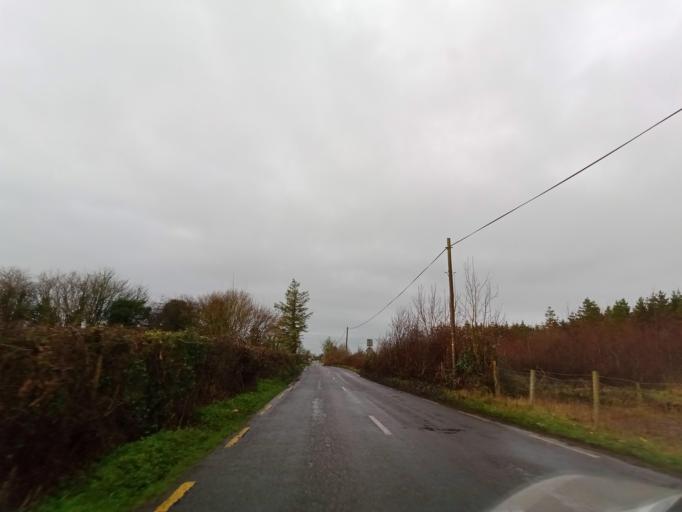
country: IE
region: Leinster
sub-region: Kilkenny
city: Callan
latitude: 52.5701
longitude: -7.4249
